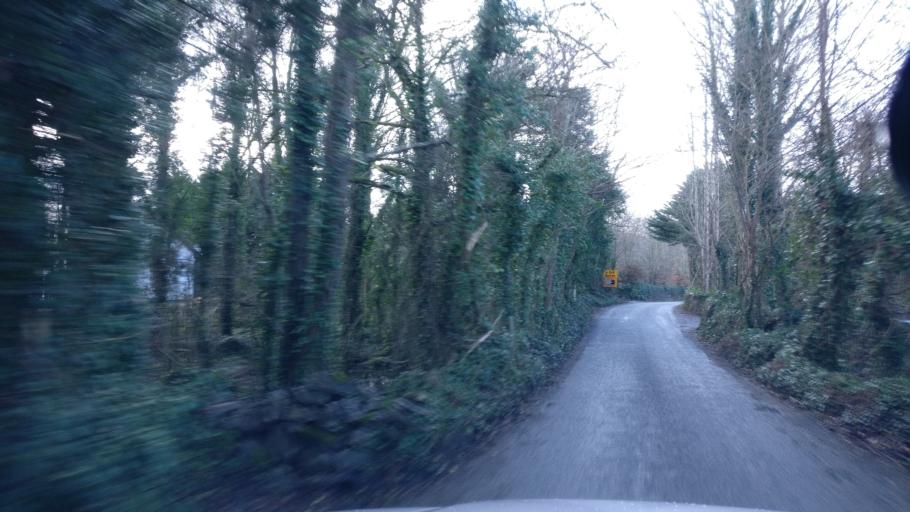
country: IE
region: Connaught
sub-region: County Galway
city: Oranmore
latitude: 53.2444
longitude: -8.9160
